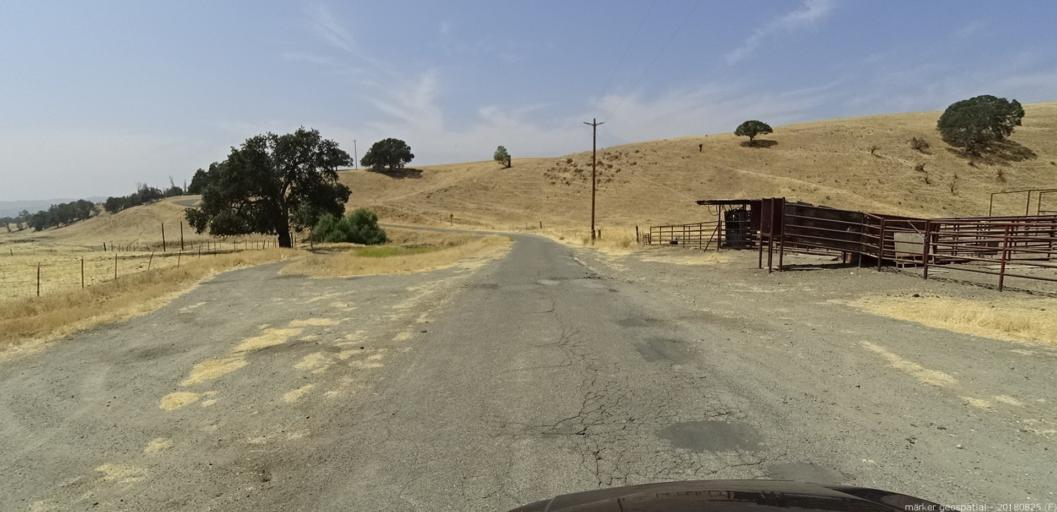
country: US
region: California
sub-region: San Luis Obispo County
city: Shandon
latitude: 35.8767
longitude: -120.3823
